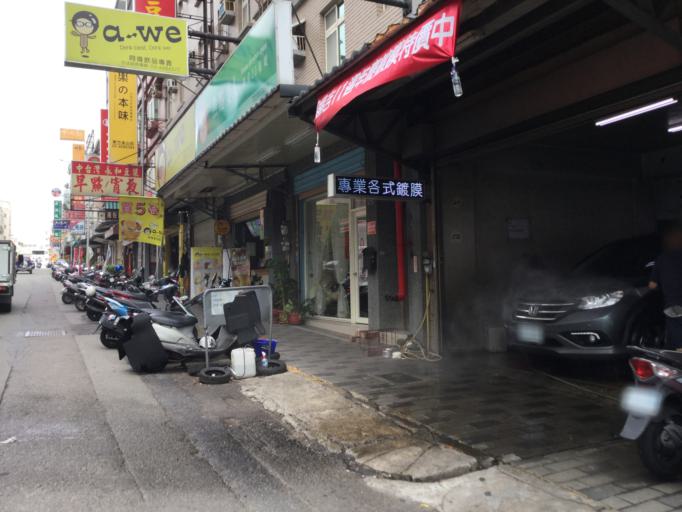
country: TW
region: Taiwan
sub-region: Hsinchu
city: Hsinchu
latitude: 24.7767
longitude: 121.0245
